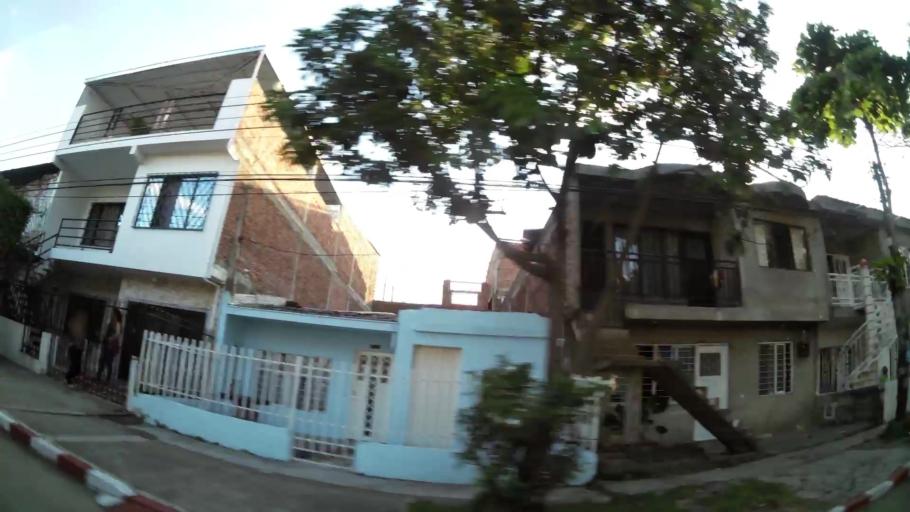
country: CO
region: Valle del Cauca
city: Cali
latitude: 3.4111
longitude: -76.5043
